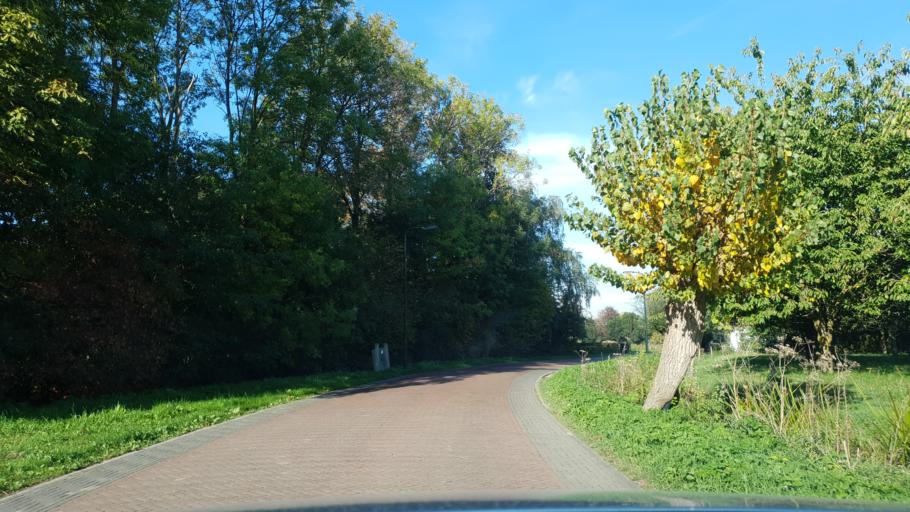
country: NL
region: Gelderland
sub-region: Gemeente Beuningen
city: Beuningen
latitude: 51.8605
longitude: 5.7450
